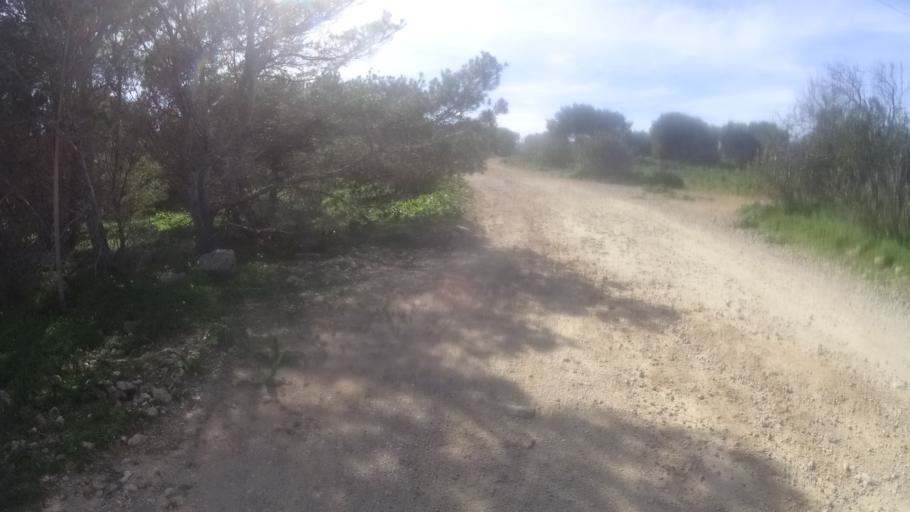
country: MT
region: Il-Qala
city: Qala
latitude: 36.0127
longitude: 14.3328
